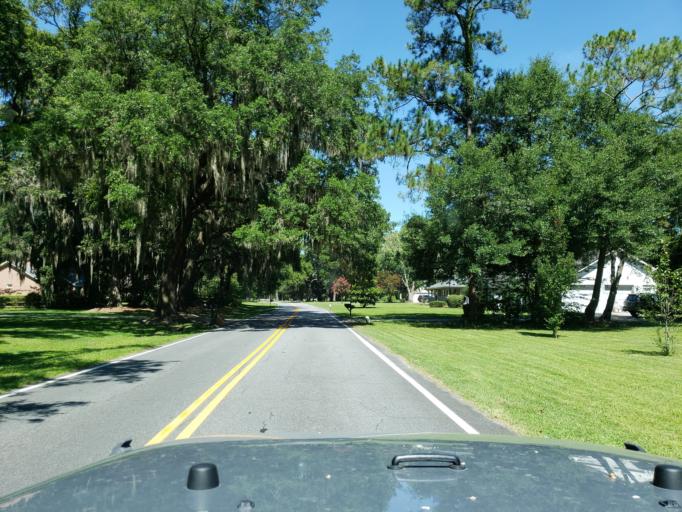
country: US
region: Georgia
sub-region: Chatham County
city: Georgetown
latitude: 31.9709
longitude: -81.2212
